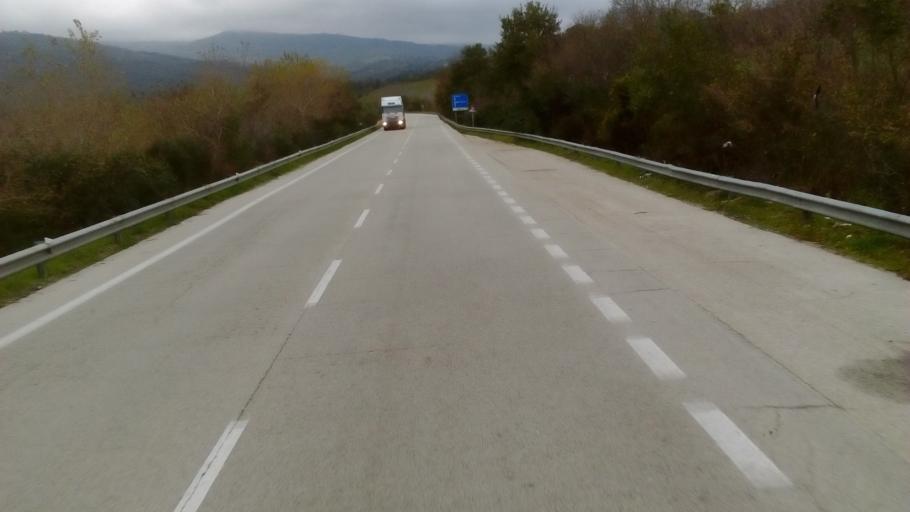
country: IT
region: Abruzzo
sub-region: Provincia di Chieti
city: Tufillo
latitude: 41.8971
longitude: 14.6271
